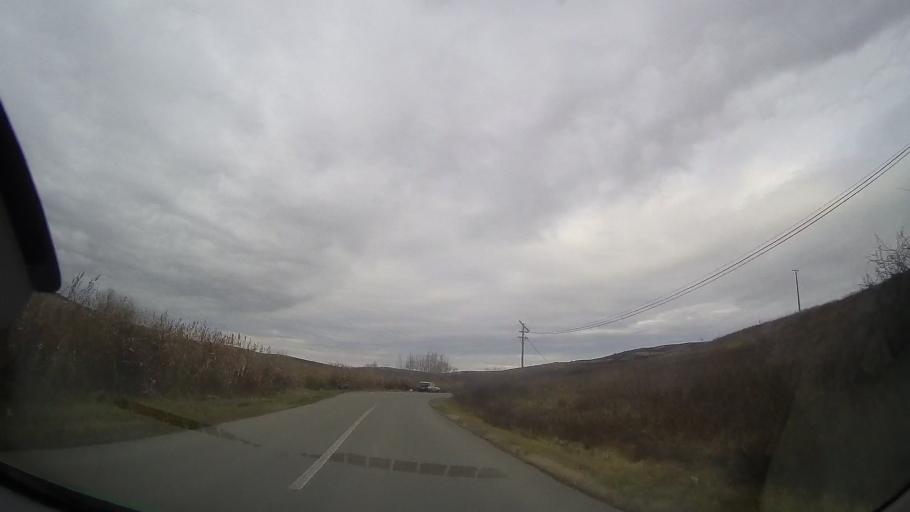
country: RO
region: Mures
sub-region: Comuna Faragau
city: Faragau
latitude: 46.7452
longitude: 24.5322
